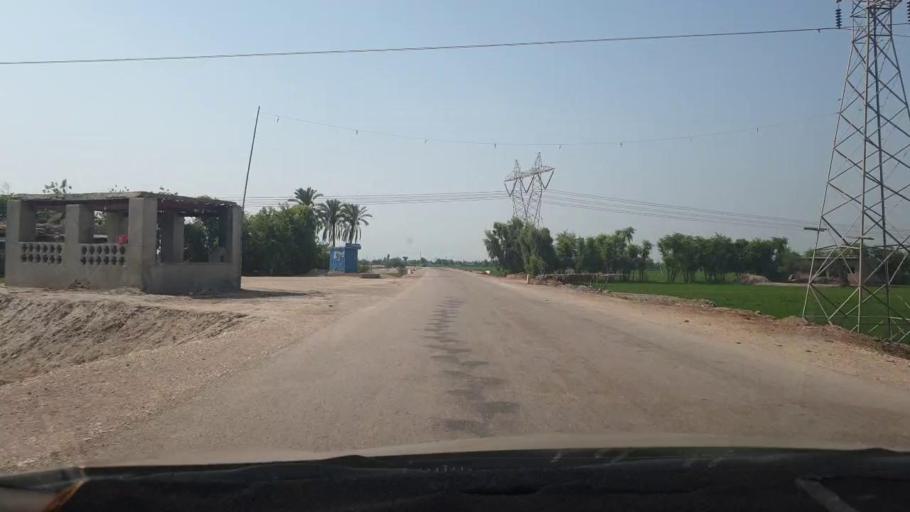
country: PK
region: Sindh
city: Larkana
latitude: 27.6070
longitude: 68.2401
